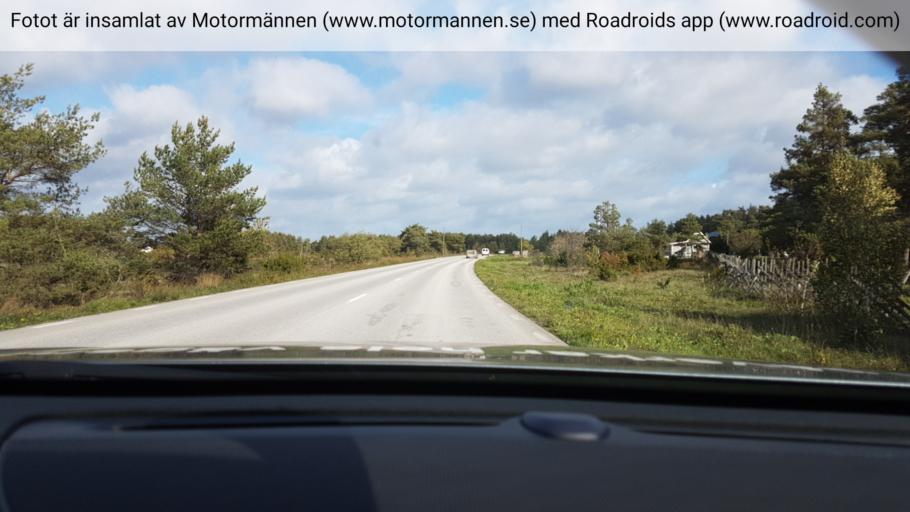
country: SE
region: Gotland
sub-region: Gotland
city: Slite
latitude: 57.8885
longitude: 19.0897
